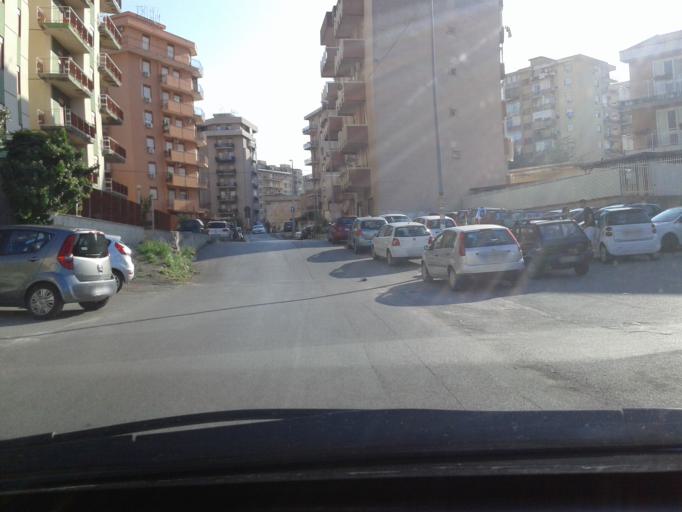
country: IT
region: Sicily
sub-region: Palermo
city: Palermo
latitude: 38.1039
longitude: 13.3285
